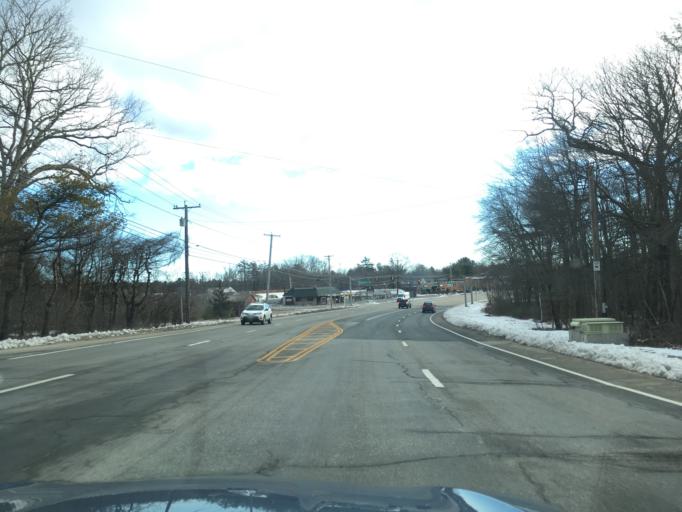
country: US
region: Rhode Island
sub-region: Kent County
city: West Warwick
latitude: 41.6778
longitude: -71.5885
